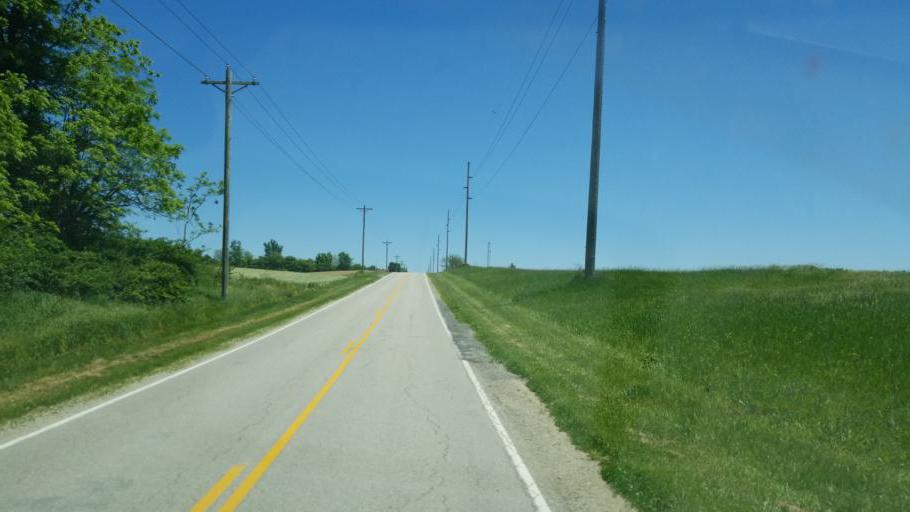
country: US
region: Ohio
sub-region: Darke County
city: Ansonia
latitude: 40.2648
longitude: -84.6452
